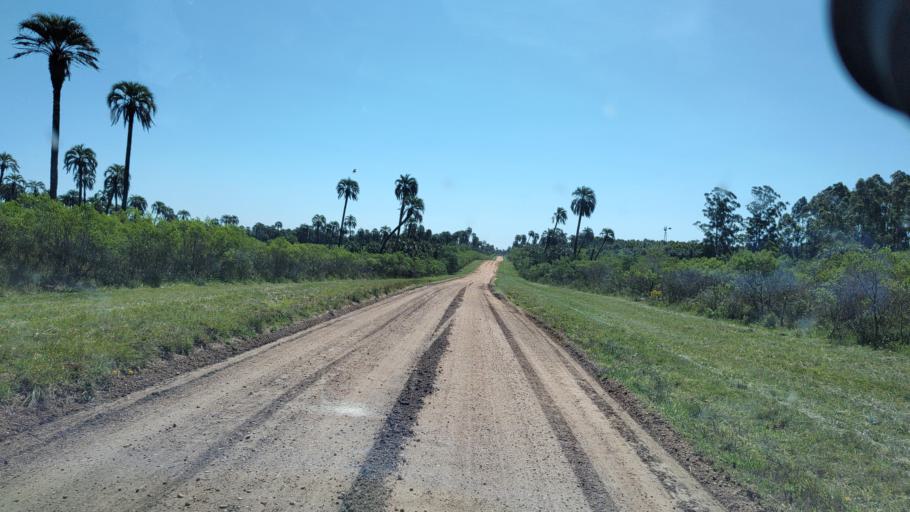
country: AR
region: Entre Rios
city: Ubajay
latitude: -31.8553
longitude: -58.2885
